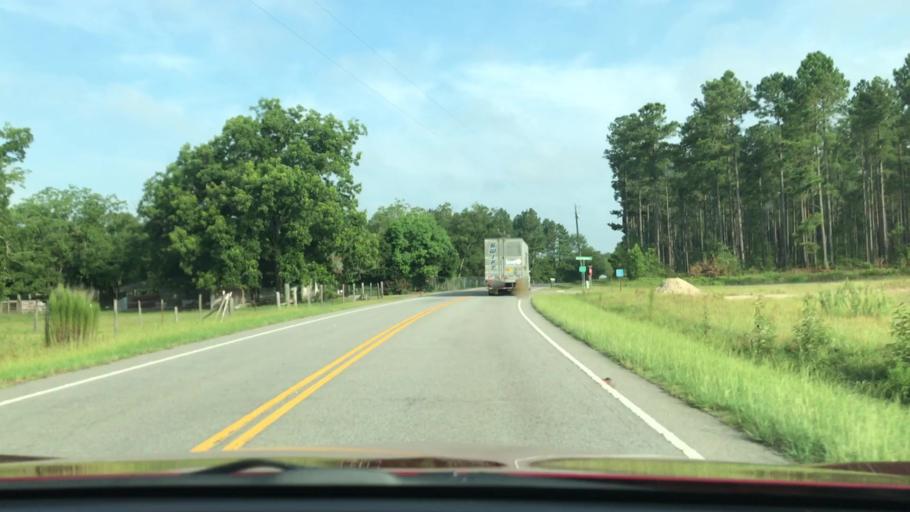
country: US
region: South Carolina
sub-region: Barnwell County
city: Williston
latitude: 33.6142
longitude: -81.2831
